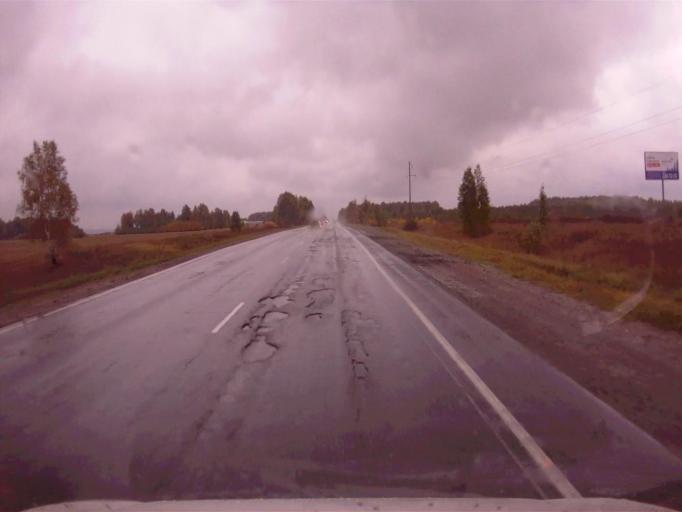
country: RU
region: Chelyabinsk
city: Novogornyy
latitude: 55.4885
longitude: 60.7014
